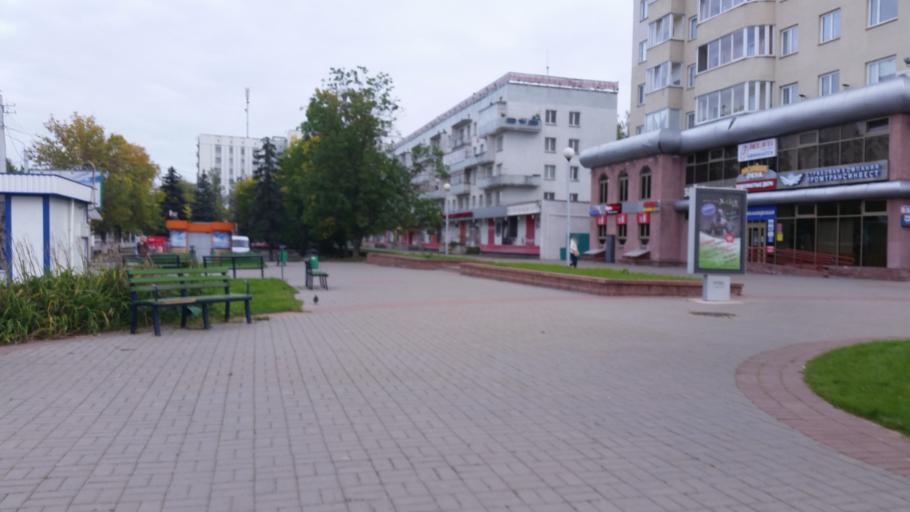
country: BY
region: Vitebsk
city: Vitebsk
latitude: 55.1737
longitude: 30.1999
